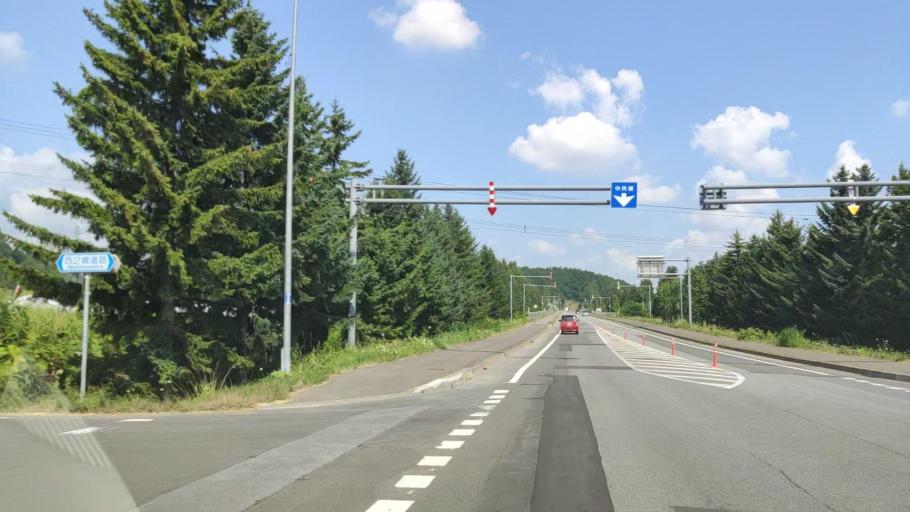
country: JP
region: Hokkaido
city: Shimo-furano
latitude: 43.4656
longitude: 142.4557
